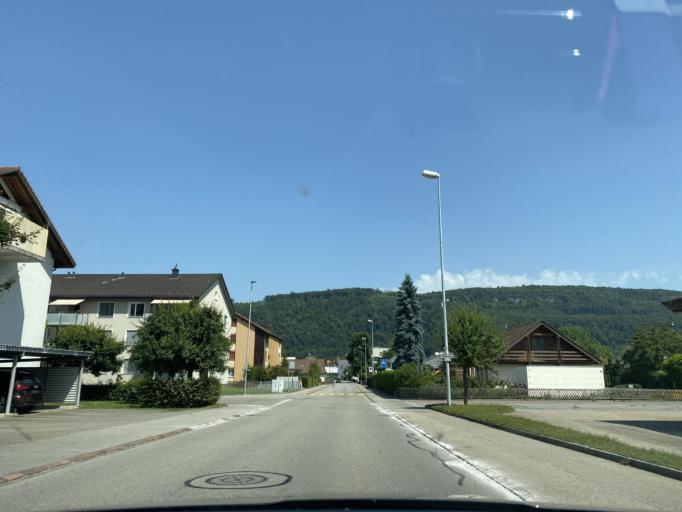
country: CH
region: Aargau
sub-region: Bezirk Zofingen
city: Rothrist
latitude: 47.3027
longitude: 7.8773
